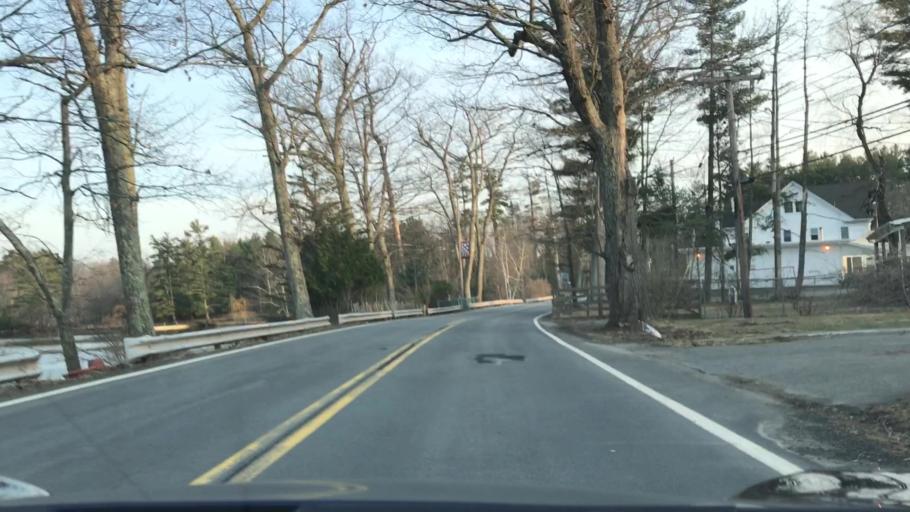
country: US
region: New York
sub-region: Sullivan County
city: Liberty
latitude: 41.6809
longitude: -74.9934
